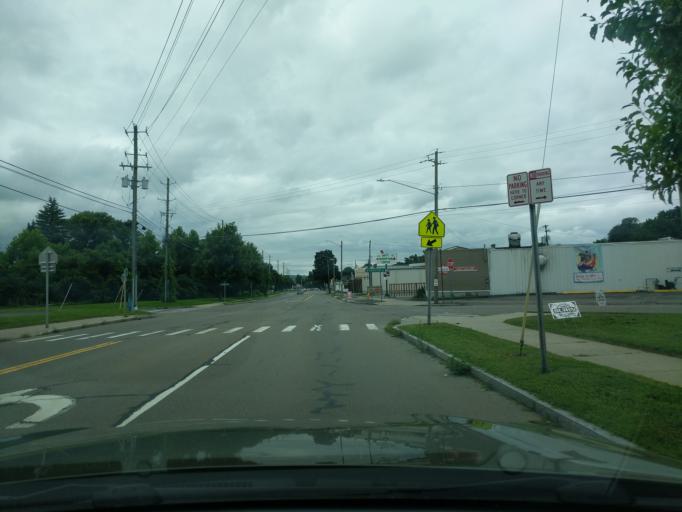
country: US
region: New York
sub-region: Chemung County
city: Elmira Heights
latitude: 42.1123
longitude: -76.8208
